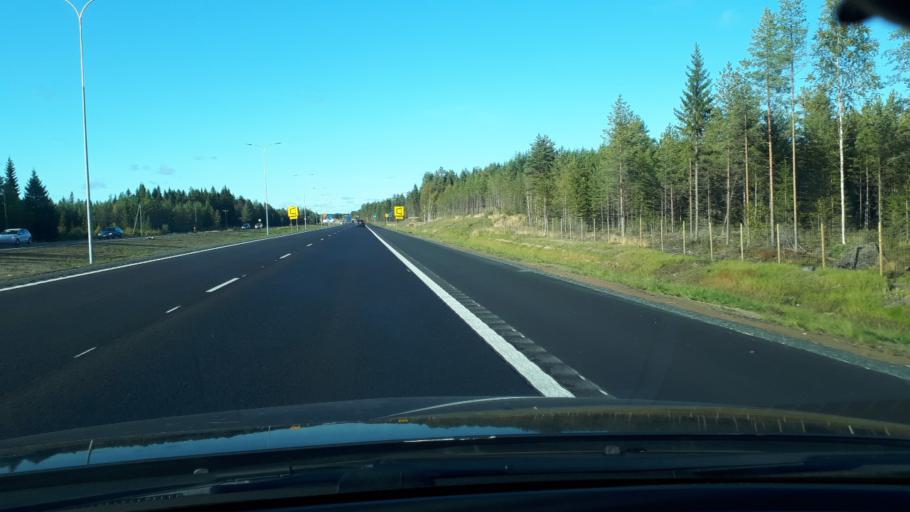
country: FI
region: Northern Ostrobothnia
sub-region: Oulu
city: Haukipudas
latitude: 65.1808
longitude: 25.4264
